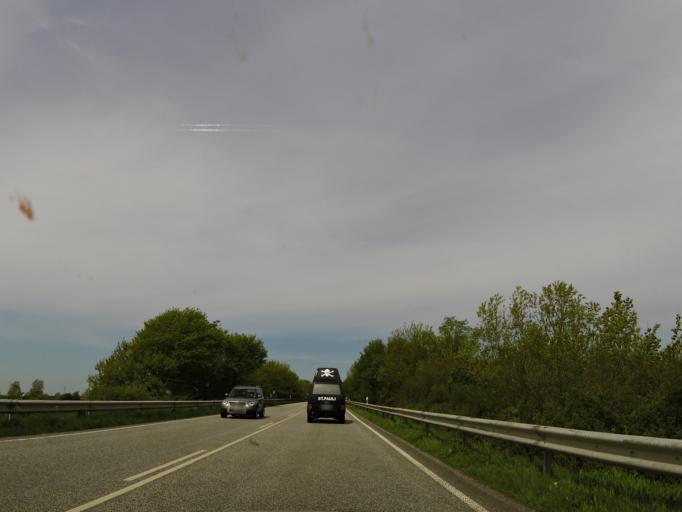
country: DE
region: Schleswig-Holstein
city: Groven
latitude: 54.2884
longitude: 8.9861
